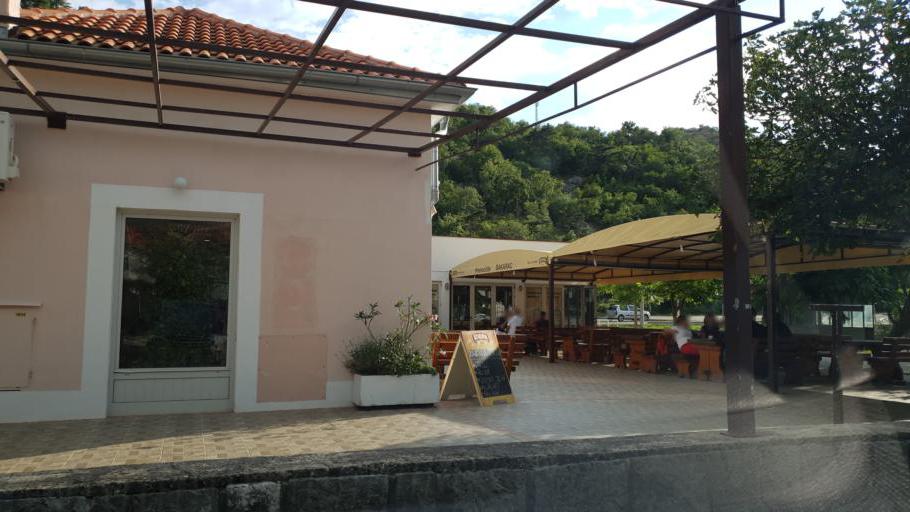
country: HR
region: Primorsko-Goranska
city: Kraljevica
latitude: 45.2794
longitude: 14.5814
